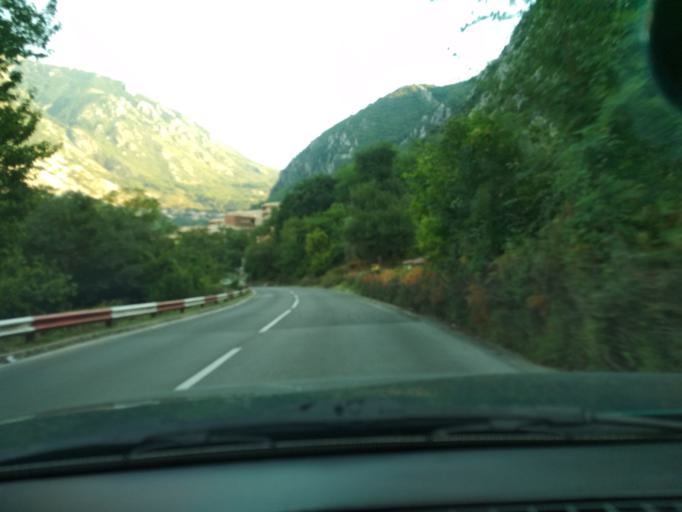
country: ME
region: Kotor
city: Kotor
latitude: 42.4205
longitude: 18.7589
